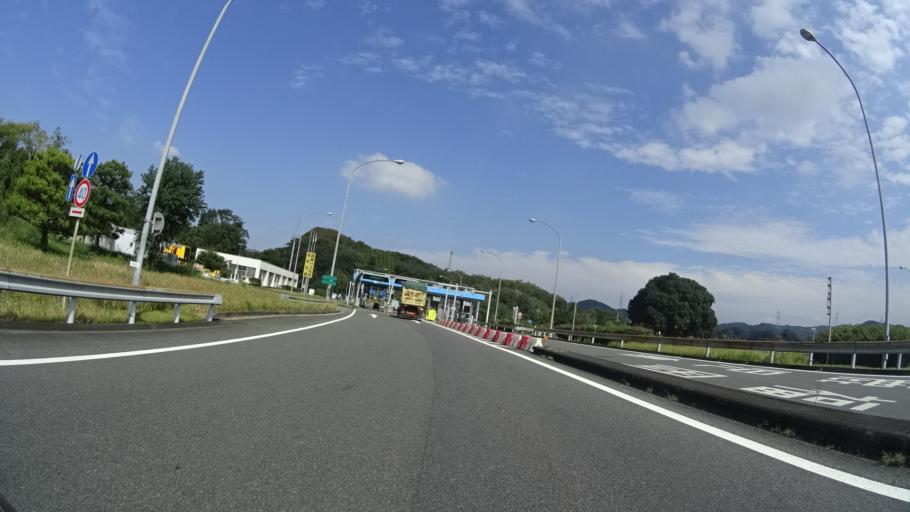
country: JP
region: Kumamoto
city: Matsubase
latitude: 32.6484
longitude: 130.7098
